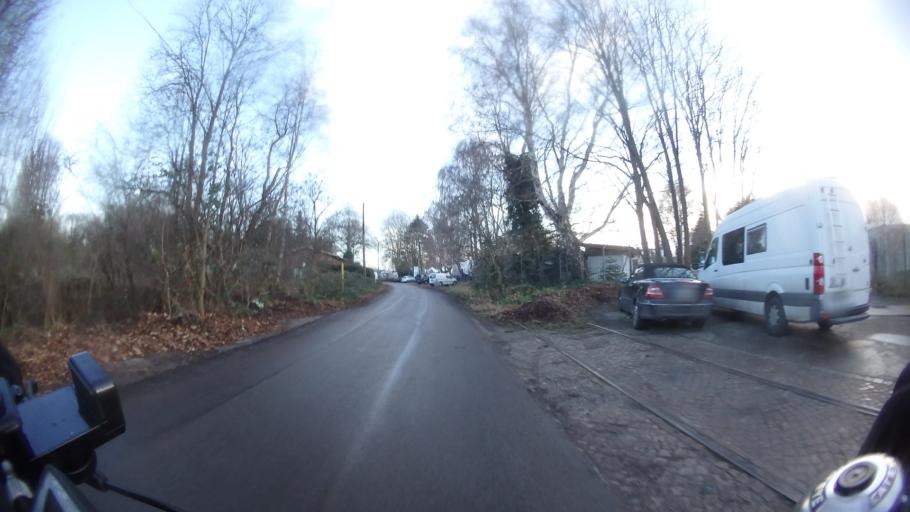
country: DE
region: Schleswig-Holstein
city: Bad Schwartau
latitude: 53.9046
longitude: 10.6967
